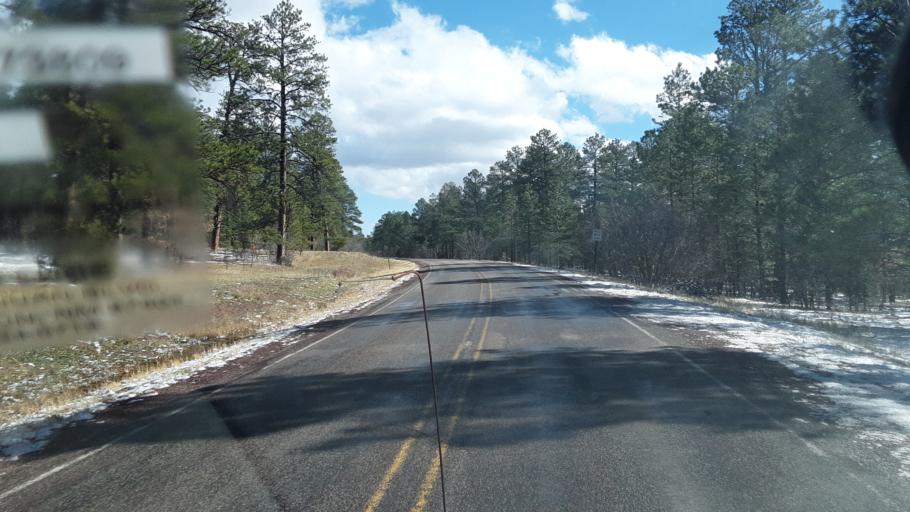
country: US
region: New Mexico
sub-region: Rio Arriba County
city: Santa Teresa
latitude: 36.1998
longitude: -106.7689
